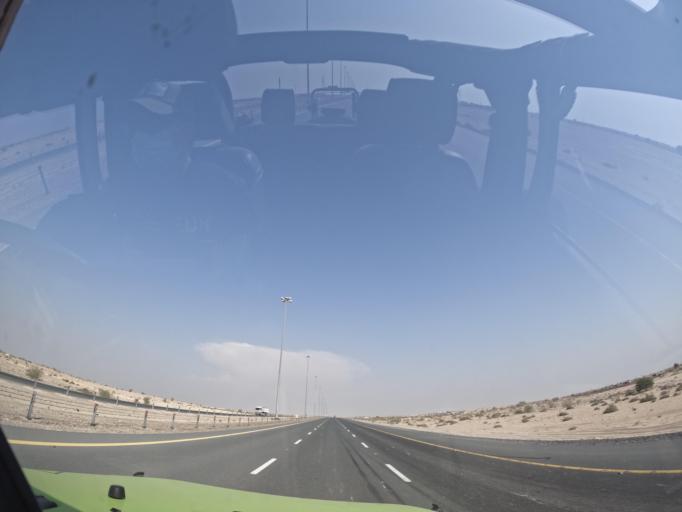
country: AE
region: Dubai
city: Dubai
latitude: 24.6764
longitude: 54.8367
